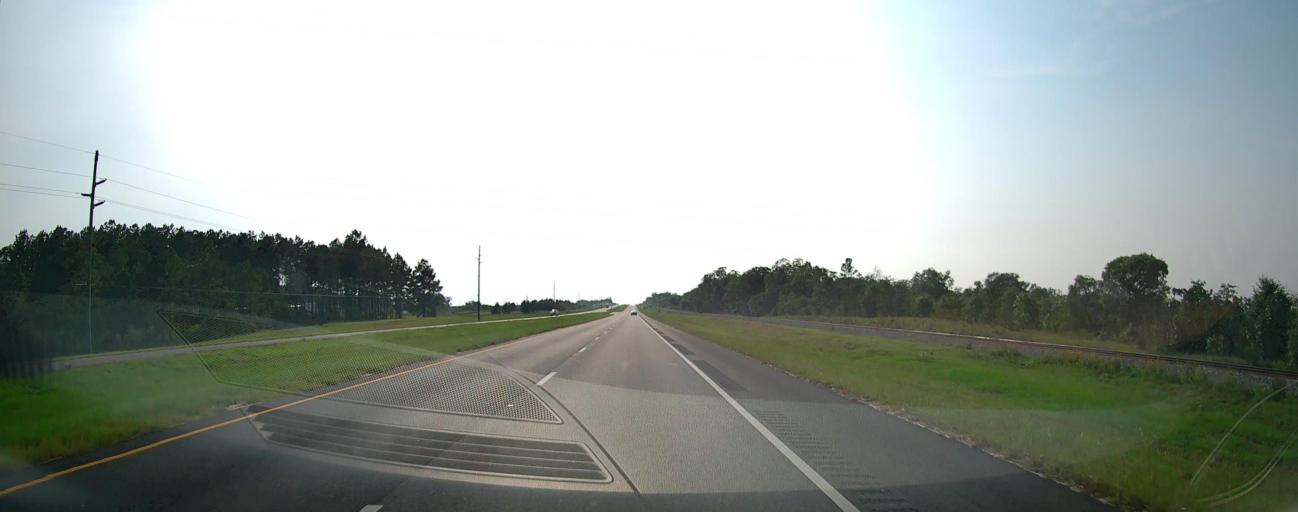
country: US
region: Georgia
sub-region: Taylor County
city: Butler
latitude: 32.5754
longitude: -84.3027
